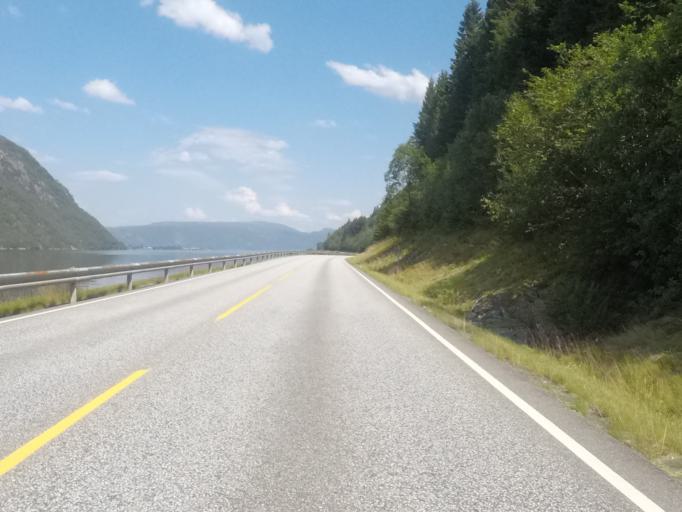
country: NO
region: Sogn og Fjordane
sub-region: Hyllestad
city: Hyllestad
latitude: 60.9897
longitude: 5.4863
